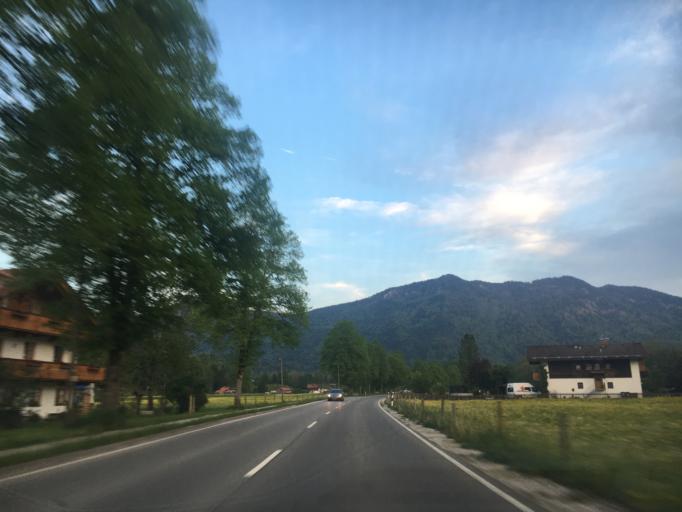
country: DE
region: Bavaria
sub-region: Upper Bavaria
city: Lenggries
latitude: 47.6434
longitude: 11.5915
